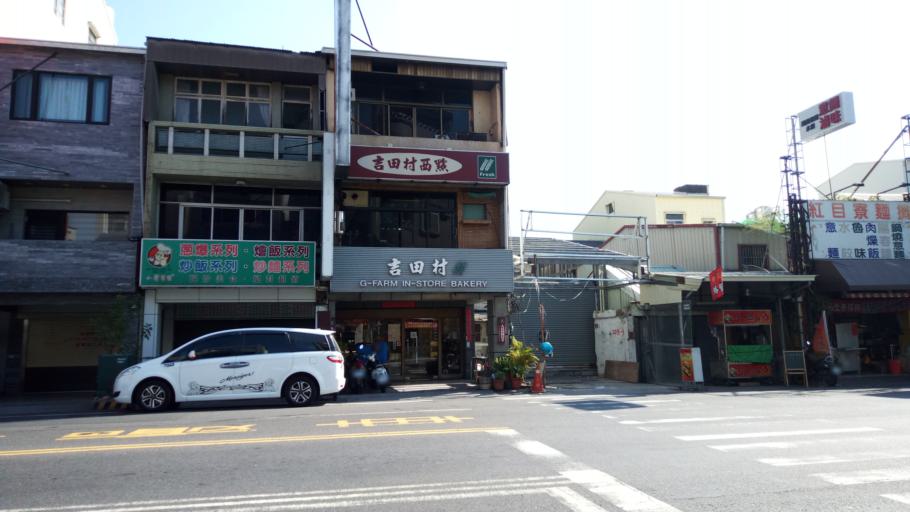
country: TW
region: Taiwan
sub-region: Tainan
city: Tainan
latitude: 23.0147
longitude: 120.1938
